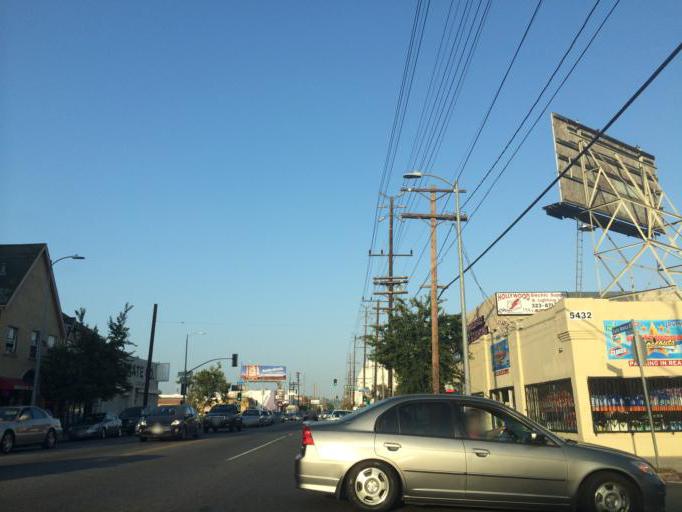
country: US
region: California
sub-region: Los Angeles County
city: Hollywood
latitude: 34.0907
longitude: -118.3079
